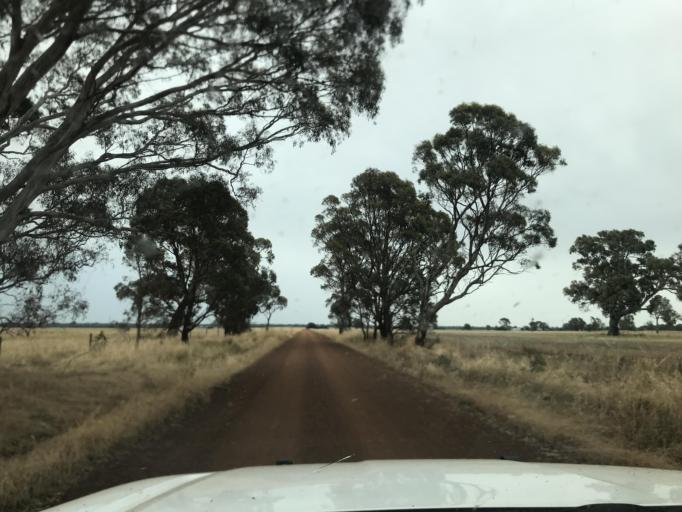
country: AU
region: Victoria
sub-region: Horsham
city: Horsham
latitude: -37.0611
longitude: 141.6166
